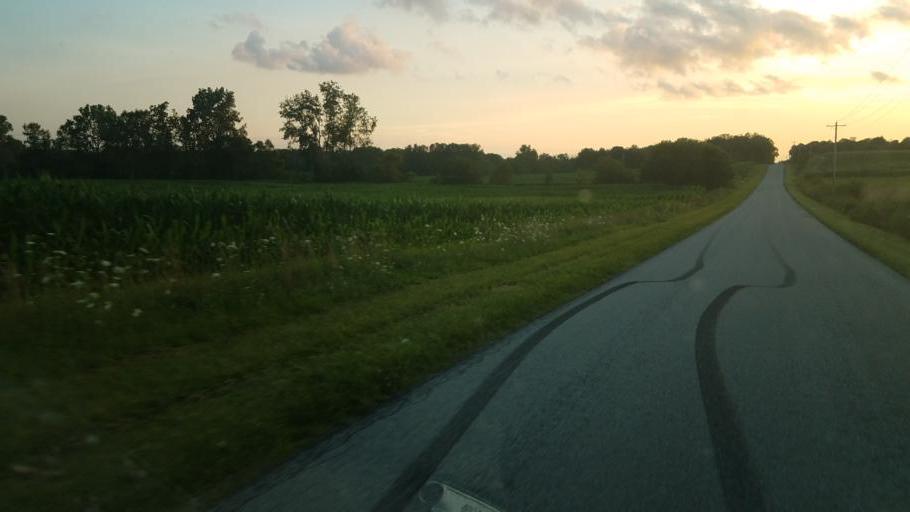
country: US
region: Ohio
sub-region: Morrow County
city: Mount Gilead
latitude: 40.5217
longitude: -82.7133
